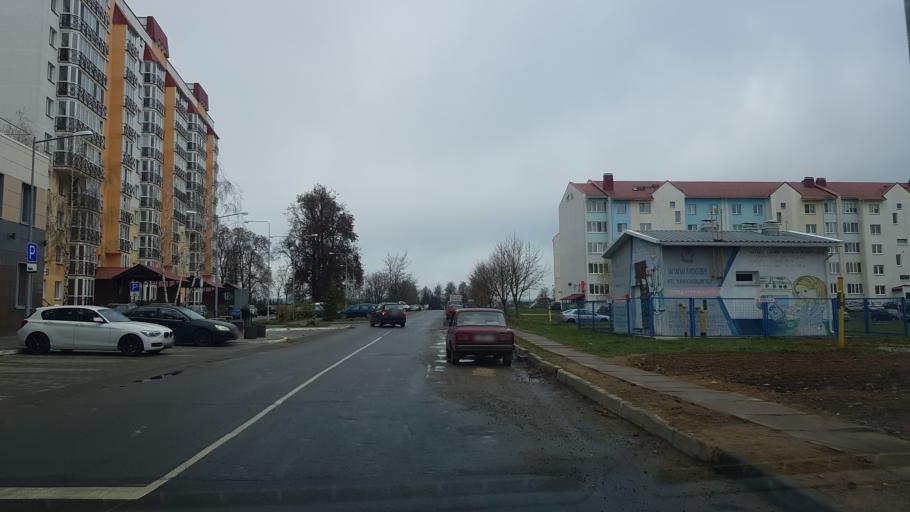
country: BY
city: Fanipol
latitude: 53.7499
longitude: 27.3297
